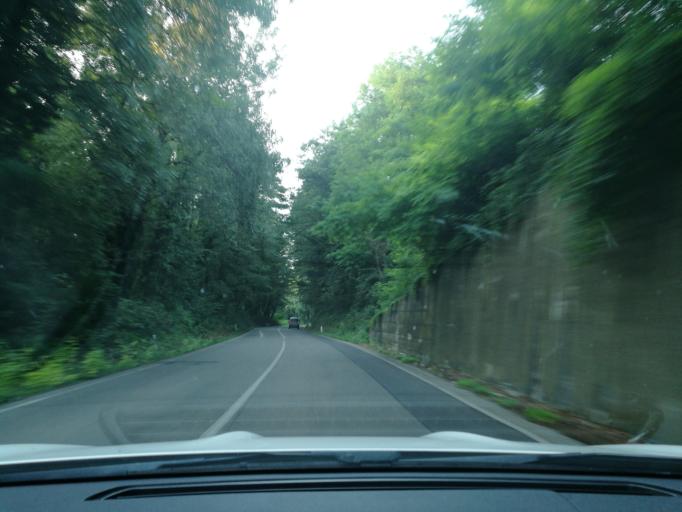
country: IT
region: Umbria
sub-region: Provincia di Terni
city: San Gemini
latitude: 42.6499
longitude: 12.5366
